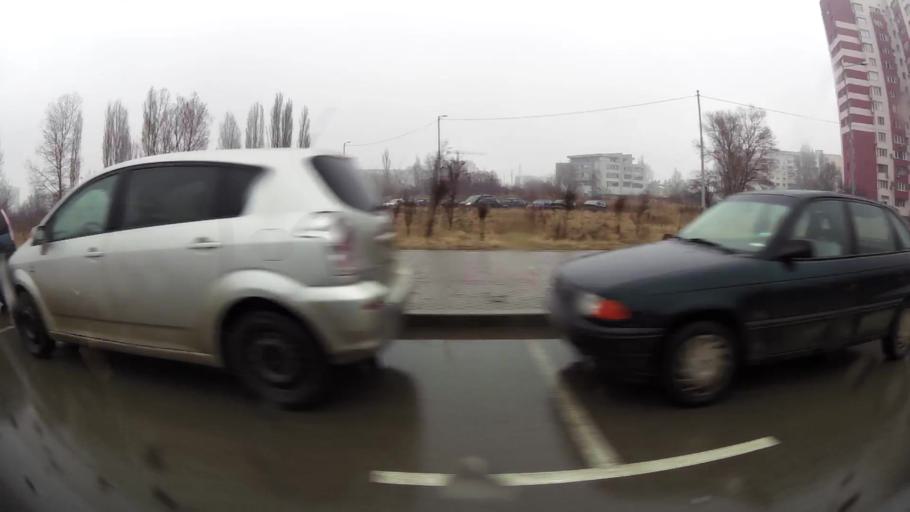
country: BG
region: Sofia-Capital
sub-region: Stolichna Obshtina
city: Sofia
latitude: 42.6554
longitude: 23.3948
